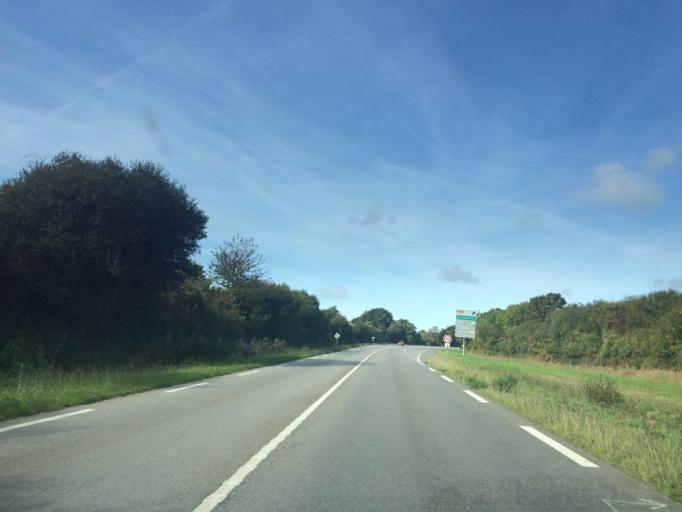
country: FR
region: Pays de la Loire
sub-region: Departement de la Loire-Atlantique
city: Port-Saint-Pere
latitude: 47.1300
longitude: -1.7479
